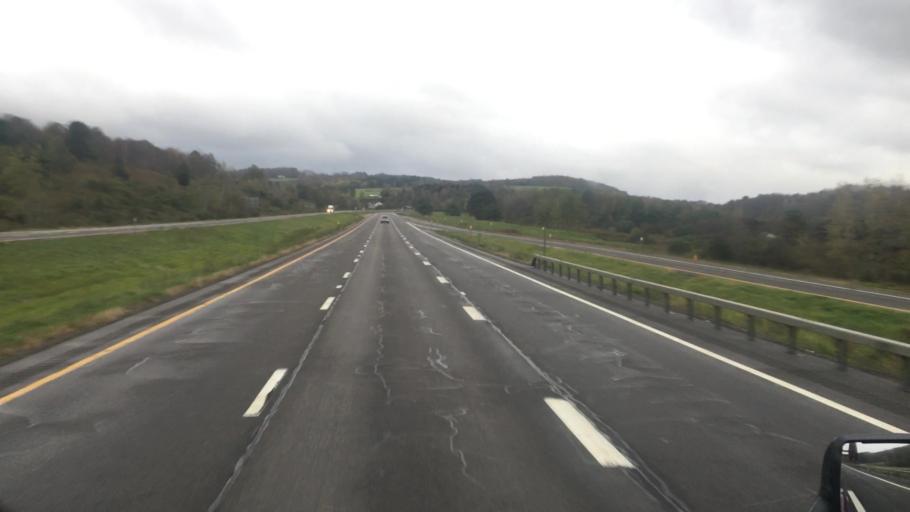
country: US
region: New York
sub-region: Chenango County
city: Bainbridge
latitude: 42.1871
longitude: -75.6399
